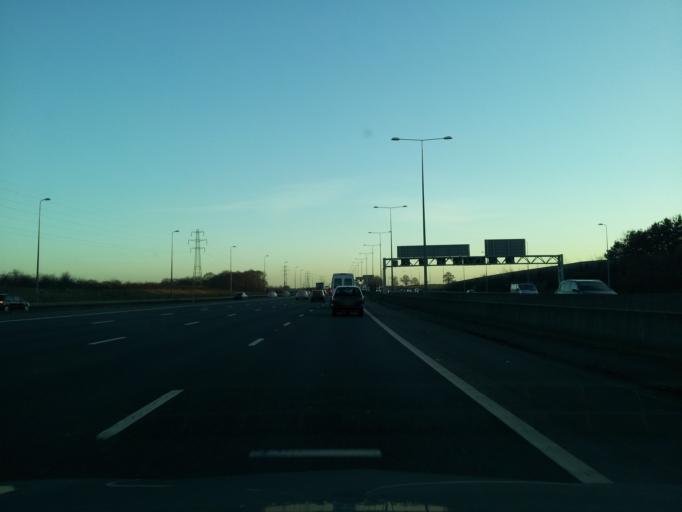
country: GB
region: England
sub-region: Luton
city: Luton
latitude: 51.8506
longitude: -0.4221
